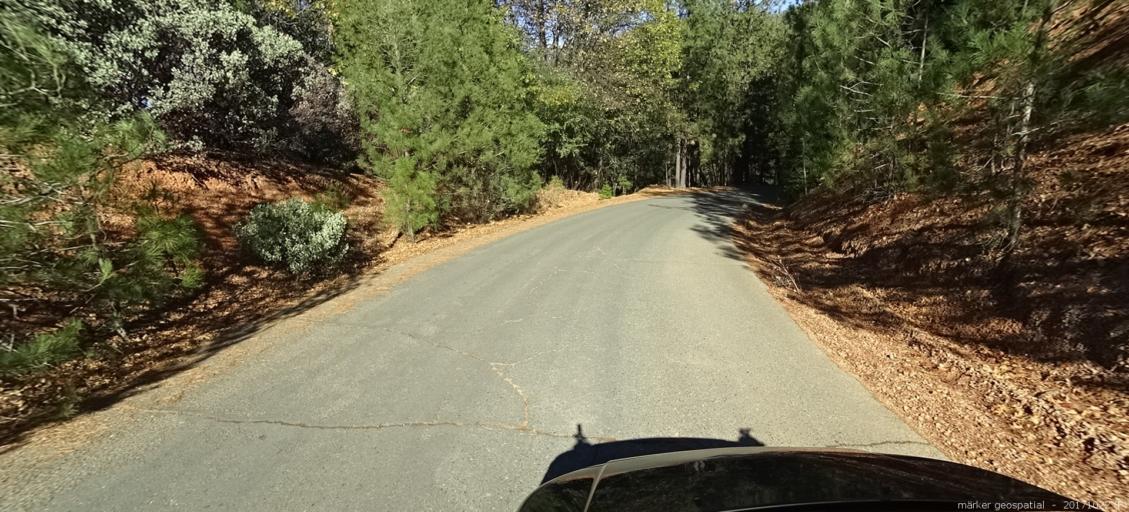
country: US
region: California
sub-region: Shasta County
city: Shasta Lake
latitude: 40.8704
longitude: -122.3656
